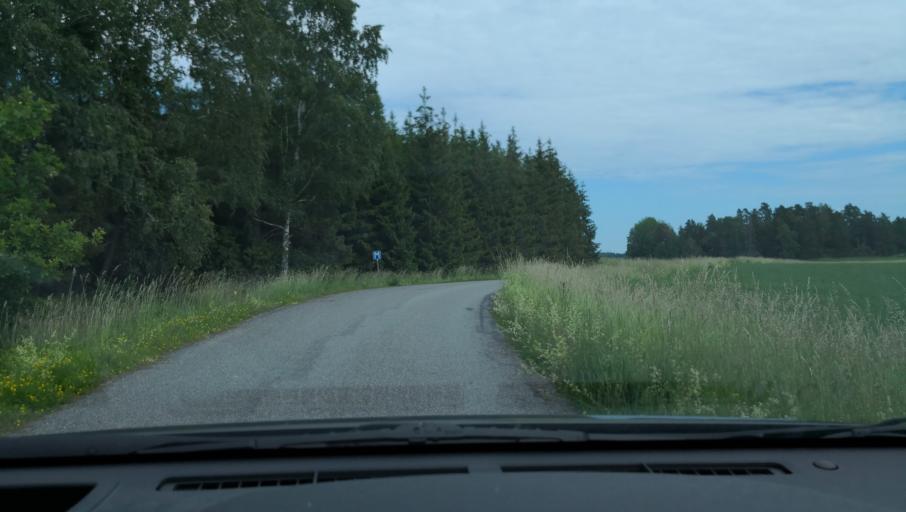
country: SE
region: Uppsala
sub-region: Enkopings Kommun
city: Orsundsbro
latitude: 59.6917
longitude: 17.2687
